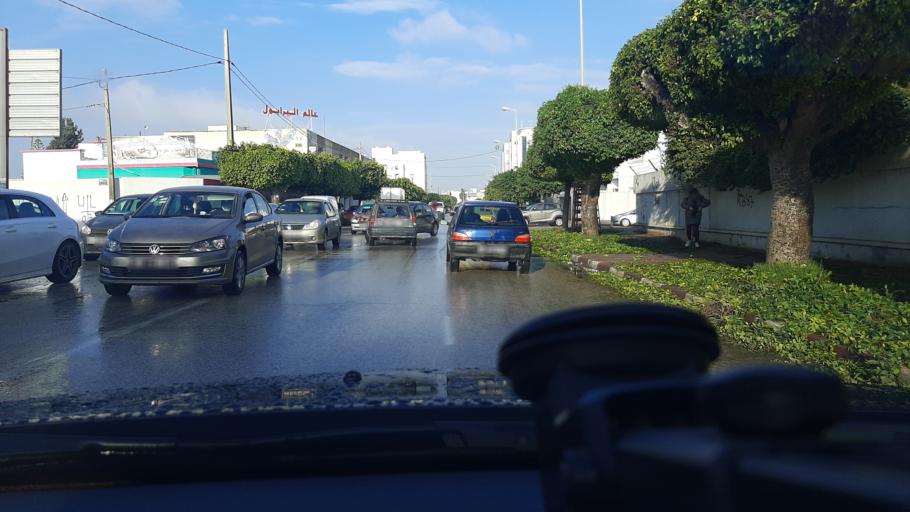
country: TN
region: Safaqis
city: Sfax
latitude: 34.7439
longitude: 10.7464
